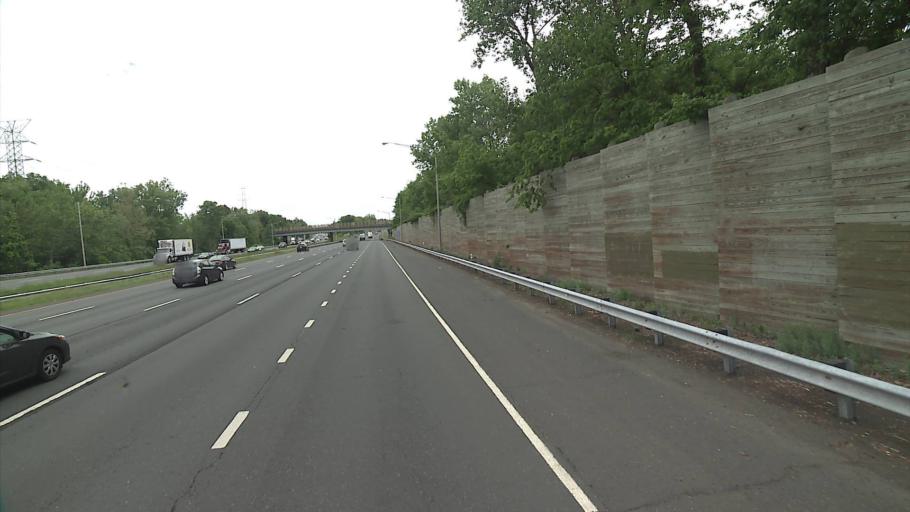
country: US
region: Connecticut
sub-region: Hartford County
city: Wethersfield
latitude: 41.6772
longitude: -72.6572
